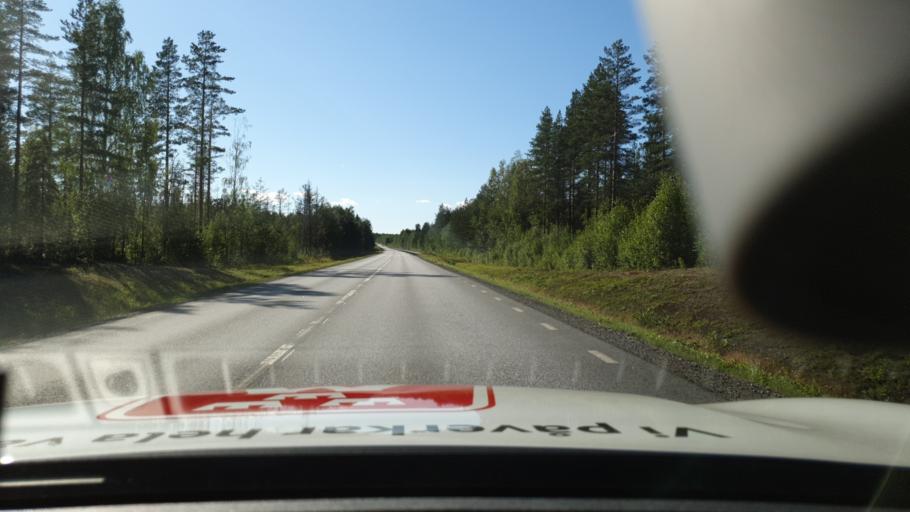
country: SE
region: Norrbotten
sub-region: Pitea Kommun
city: Rosvik
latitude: 65.5981
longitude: 21.5814
